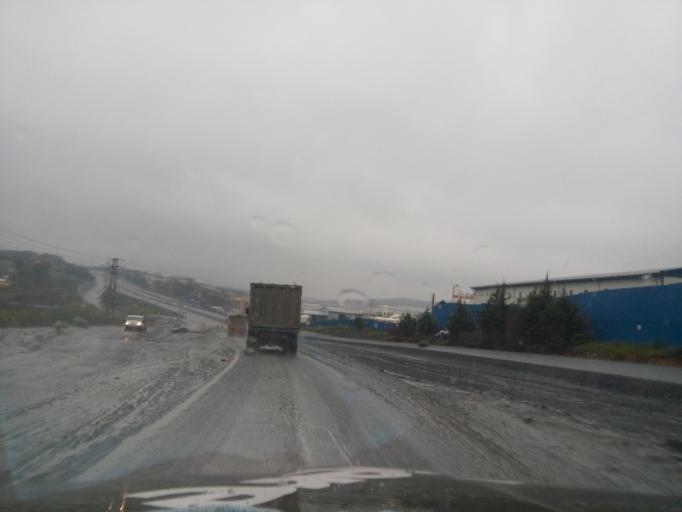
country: TR
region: Istanbul
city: Kemerburgaz
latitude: 41.2398
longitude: 28.8132
